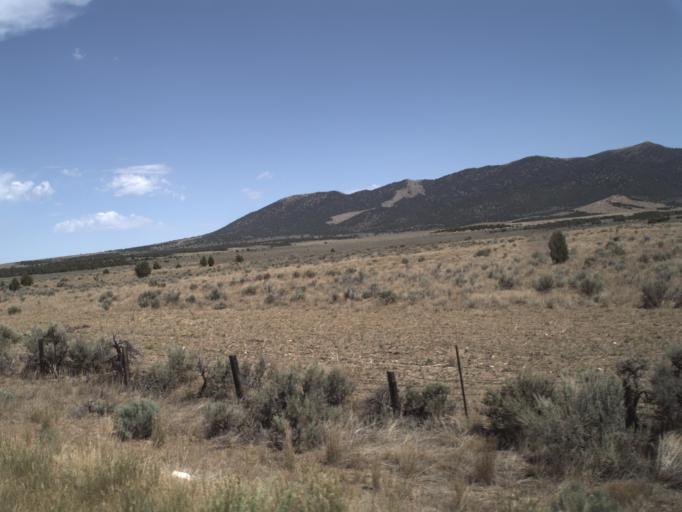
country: US
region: Utah
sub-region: Utah County
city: Genola
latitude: 39.9414
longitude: -112.1902
